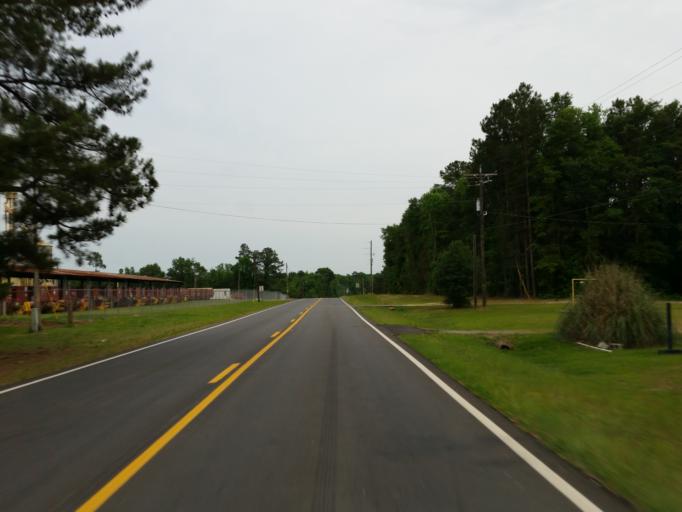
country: US
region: Georgia
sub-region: Dooly County
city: Unadilla
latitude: 32.2773
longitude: -83.7413
